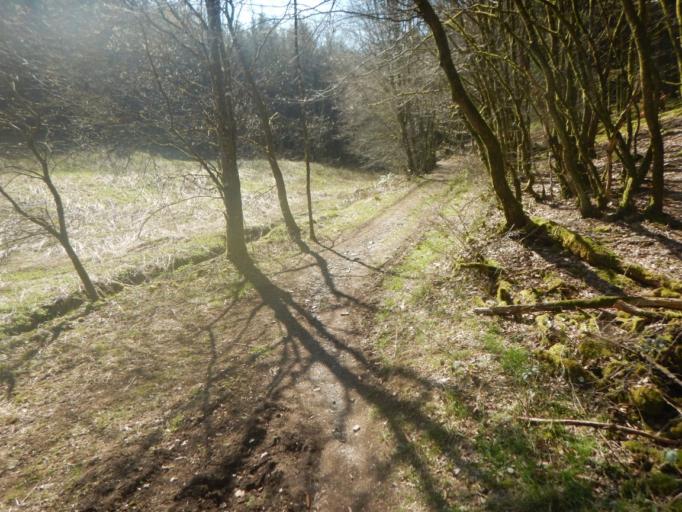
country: LU
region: Diekirch
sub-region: Canton de Wiltz
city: Wiltz
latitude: 49.9549
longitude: 5.9498
